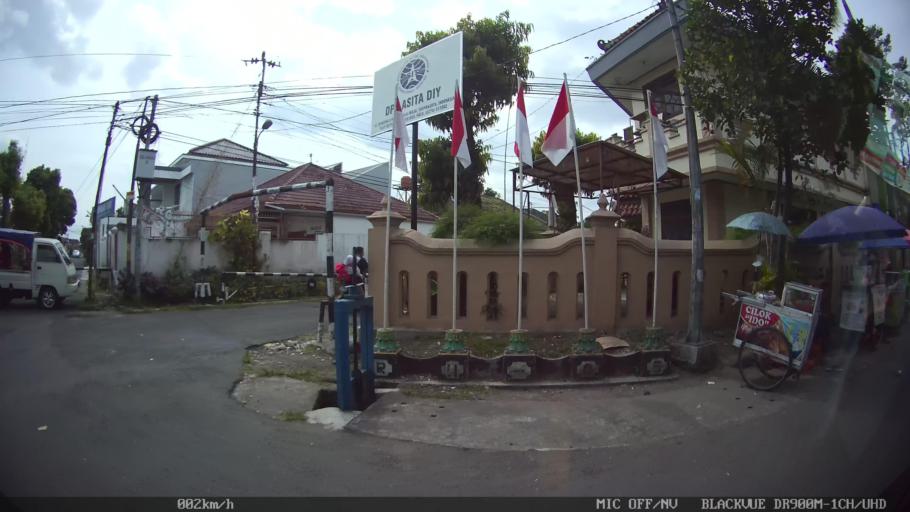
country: ID
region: Daerah Istimewa Yogyakarta
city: Yogyakarta
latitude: -7.7967
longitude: 110.3945
